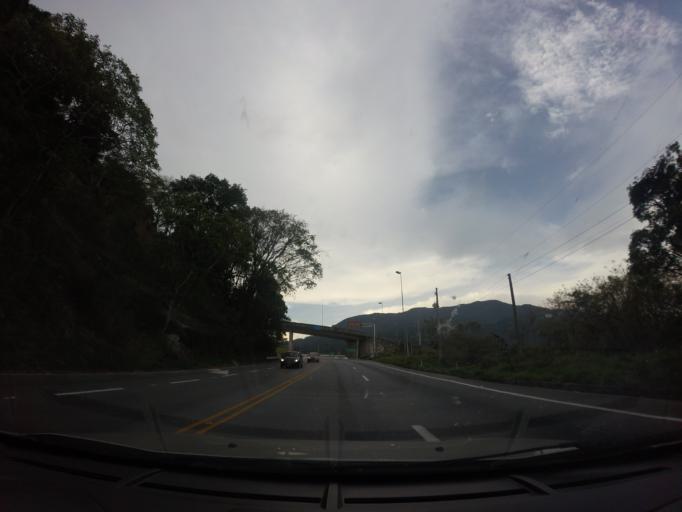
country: BR
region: Sao Paulo
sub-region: Campos Do Jordao
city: Campos do Jordao
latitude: -22.8330
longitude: -45.6241
